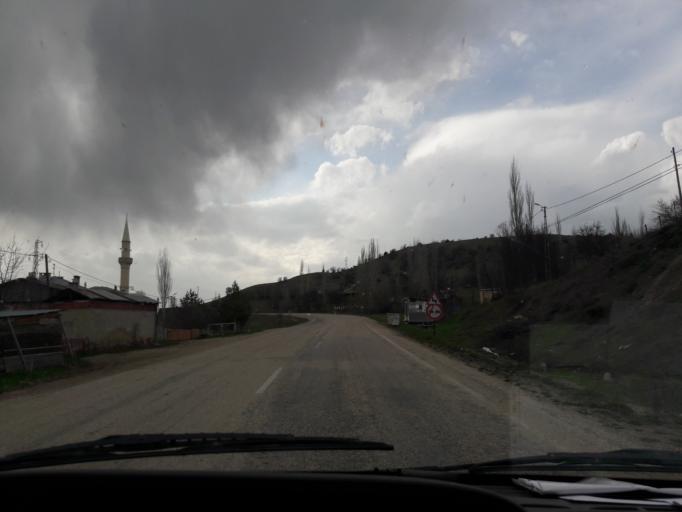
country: TR
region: Giresun
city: Alucra
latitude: 40.2971
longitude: 38.8034
